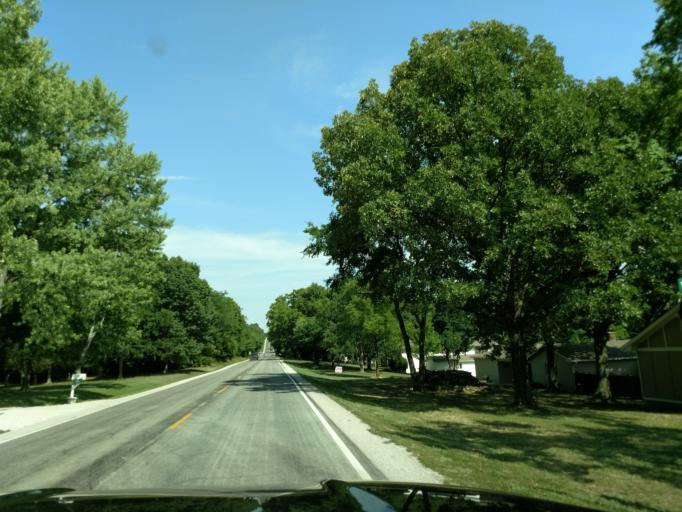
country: US
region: Missouri
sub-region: Barry County
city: Shell Knob
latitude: 36.6161
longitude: -93.6018
